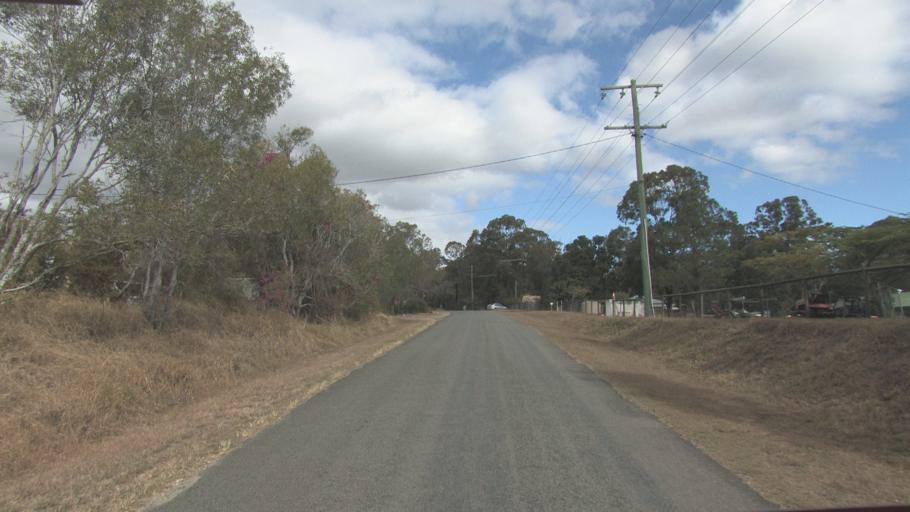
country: AU
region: Queensland
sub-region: Logan
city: Cedar Vale
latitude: -27.8879
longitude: 153.0235
